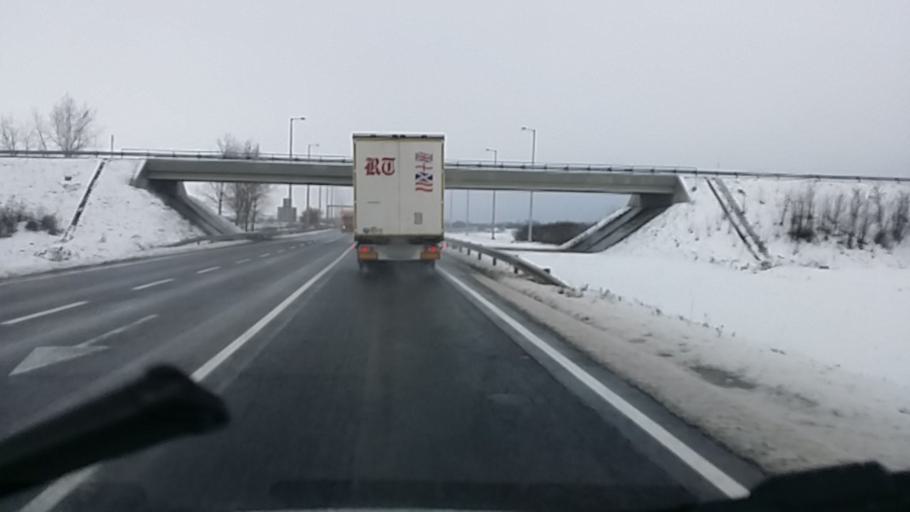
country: HU
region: Gyor-Moson-Sopron
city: Rajka
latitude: 48.0021
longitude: 17.1828
